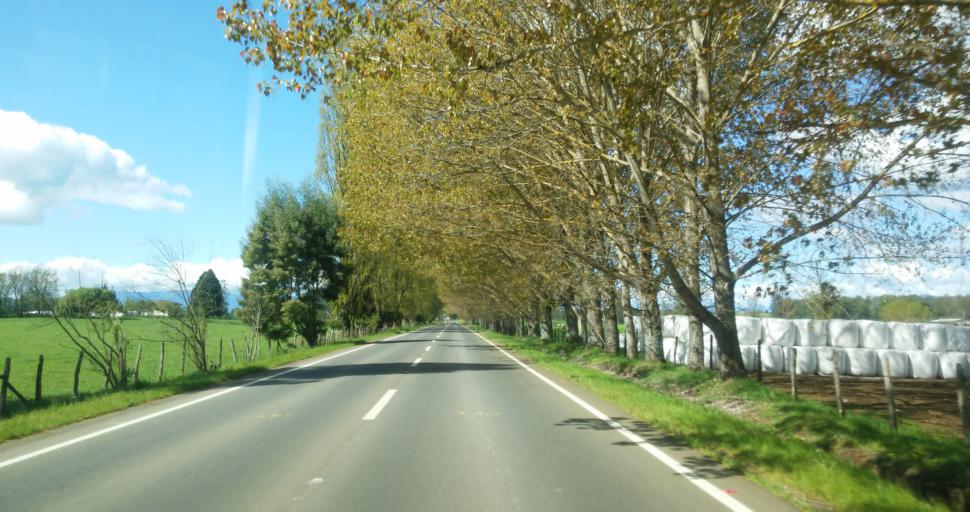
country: CL
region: Los Rios
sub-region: Provincia del Ranco
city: Rio Bueno
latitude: -40.2429
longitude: -72.6129
